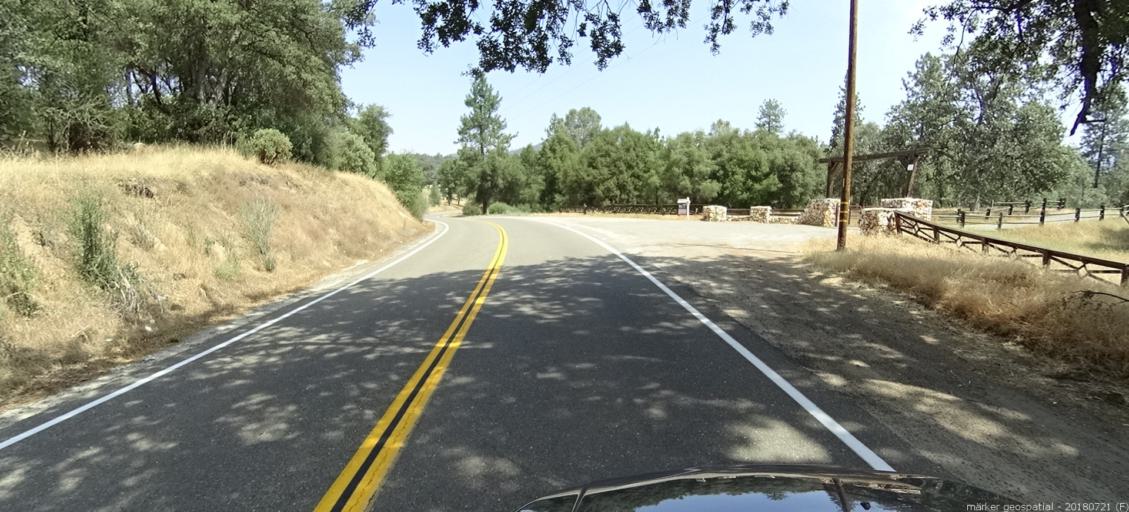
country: US
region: California
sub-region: Madera County
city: Oakhurst
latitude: 37.2302
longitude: -119.5521
